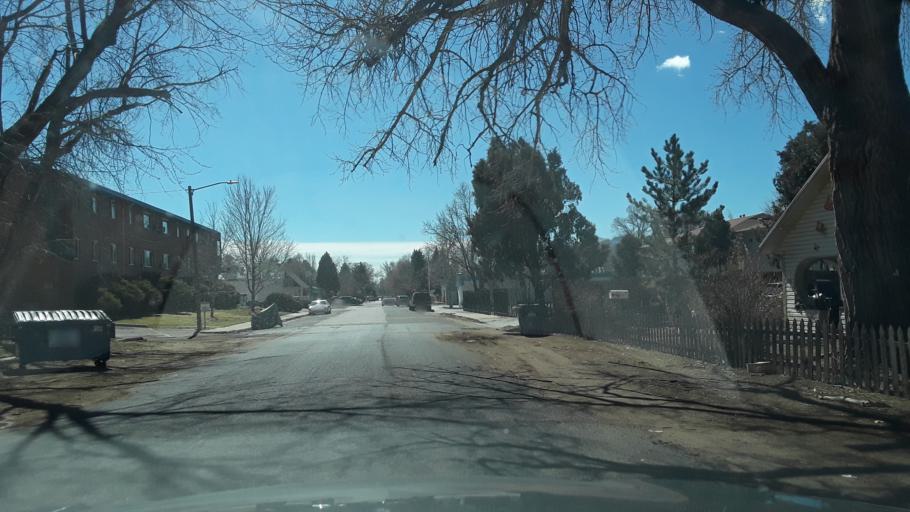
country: US
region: Colorado
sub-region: El Paso County
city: Colorado Springs
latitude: 38.8753
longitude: -104.8045
